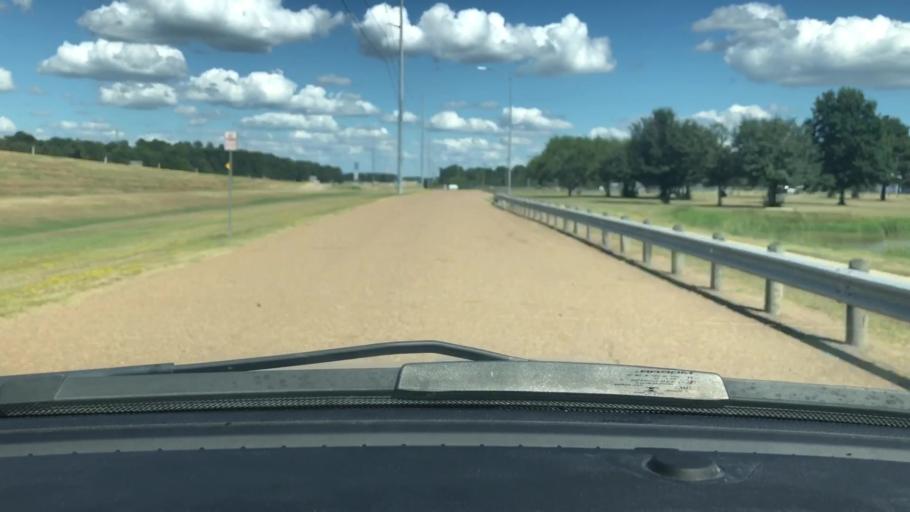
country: US
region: Texas
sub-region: Bowie County
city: Wake Village
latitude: 33.3849
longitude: -94.0898
